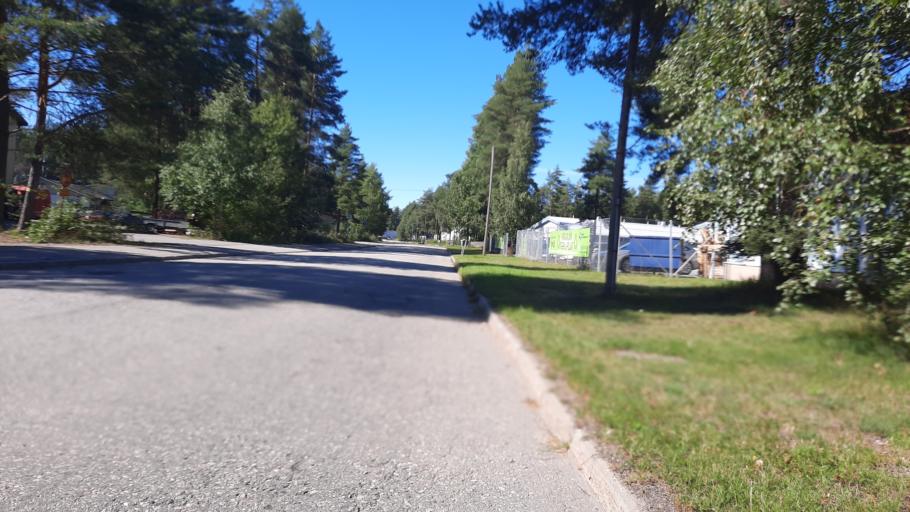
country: FI
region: North Karelia
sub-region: Joensuu
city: Joensuu
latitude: 62.6242
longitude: 29.7455
